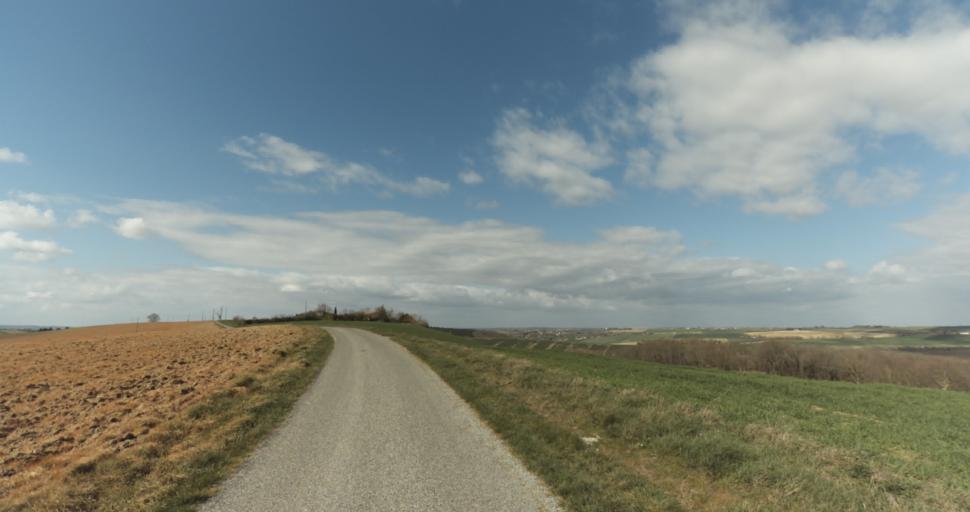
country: FR
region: Midi-Pyrenees
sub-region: Departement de la Haute-Garonne
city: Auterive
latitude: 43.3612
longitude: 1.5141
